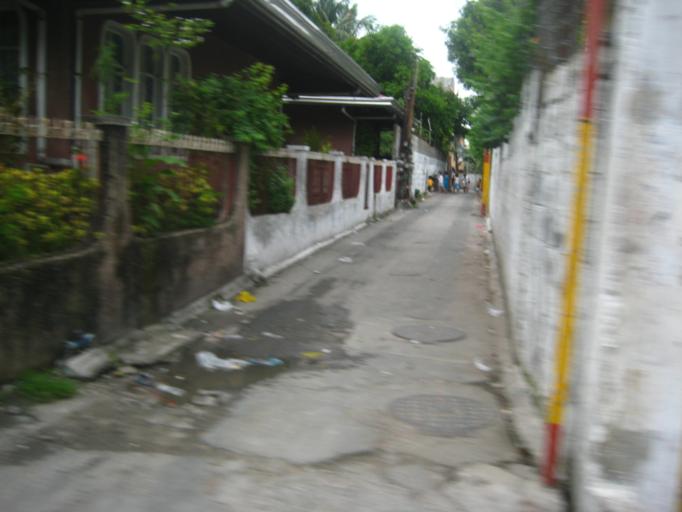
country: PH
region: Calabarzon
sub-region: Province of Rizal
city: Pateros
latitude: 14.5462
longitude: 121.0703
